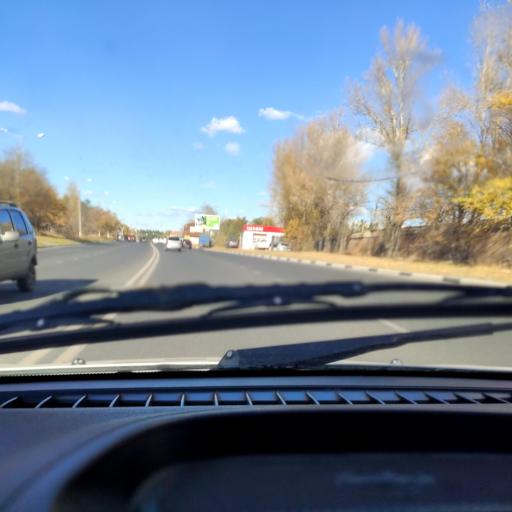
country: RU
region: Samara
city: Zhigulevsk
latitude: 53.4922
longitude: 49.4743
